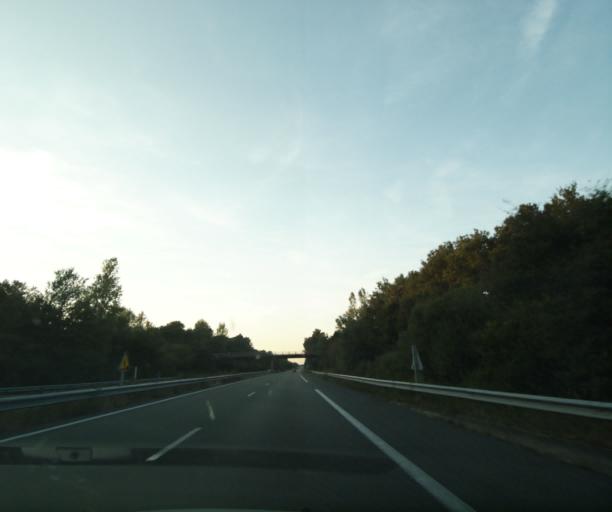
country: FR
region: Aquitaine
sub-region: Departement du Lot-et-Garonne
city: Fourques-sur-Garonne
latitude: 44.3906
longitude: 0.1970
